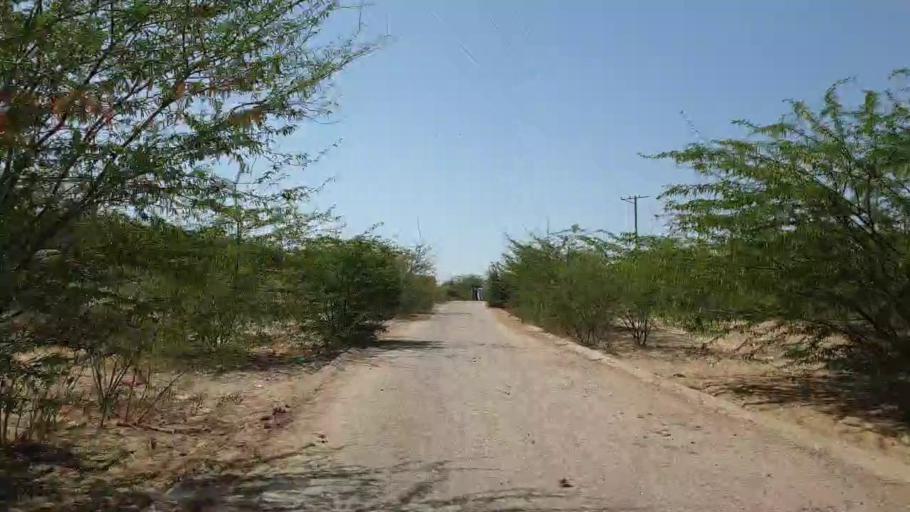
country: PK
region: Sindh
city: Umarkot
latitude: 25.1693
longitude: 69.9687
